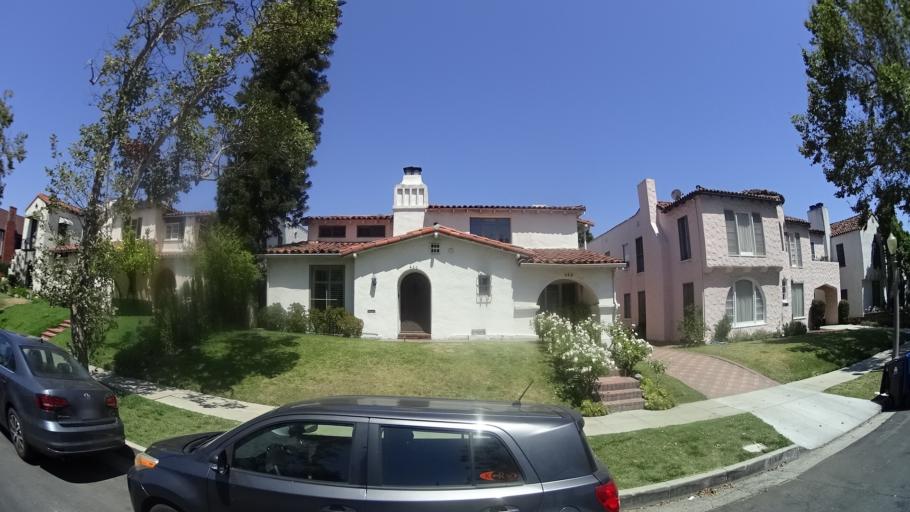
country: US
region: California
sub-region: Los Angeles County
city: West Hollywood
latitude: 34.0791
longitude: -118.3419
